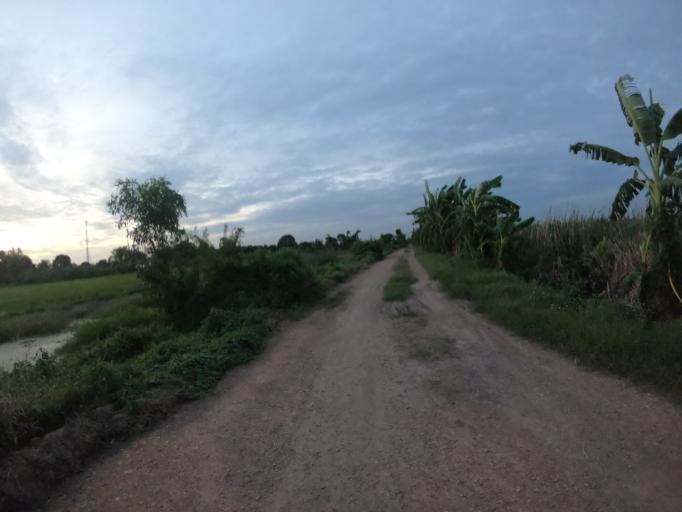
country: TH
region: Pathum Thani
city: Ban Rangsit
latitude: 14.0245
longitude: 100.8018
